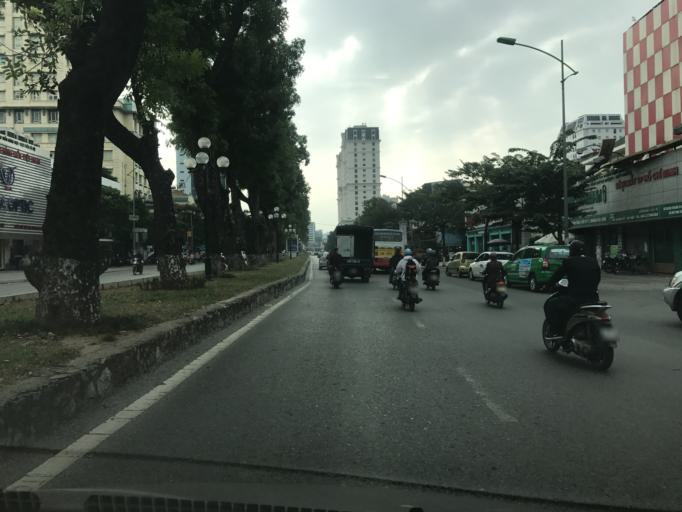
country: VN
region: Ha Noi
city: Dong Da
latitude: 21.0283
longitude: 105.8255
